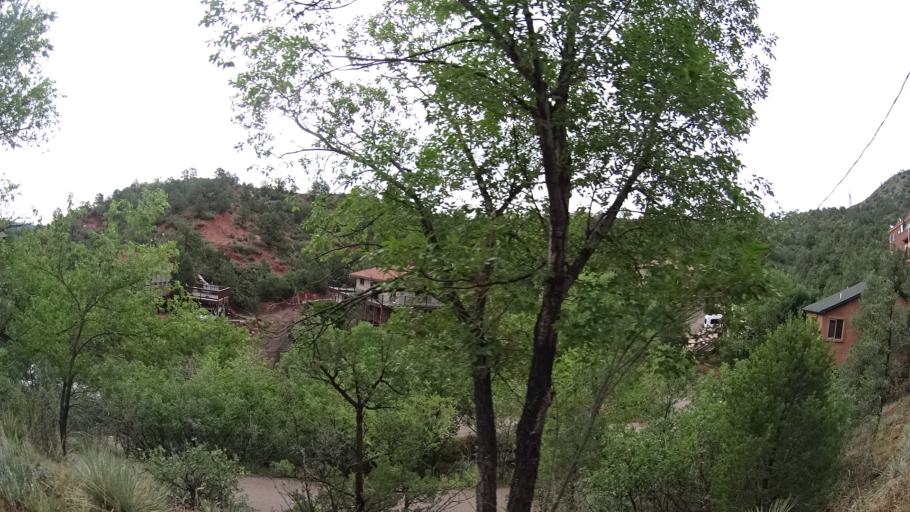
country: US
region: Colorado
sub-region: El Paso County
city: Manitou Springs
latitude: 38.8555
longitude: -104.9092
